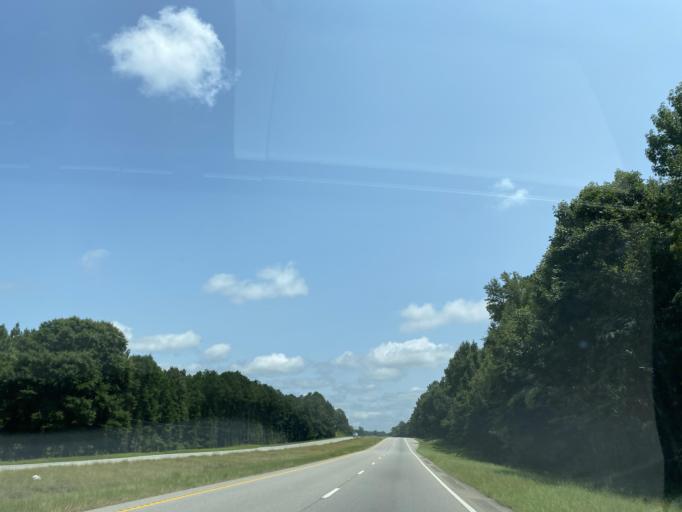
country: US
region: Georgia
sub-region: Telfair County
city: Lumber City
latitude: 31.9057
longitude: -82.6575
